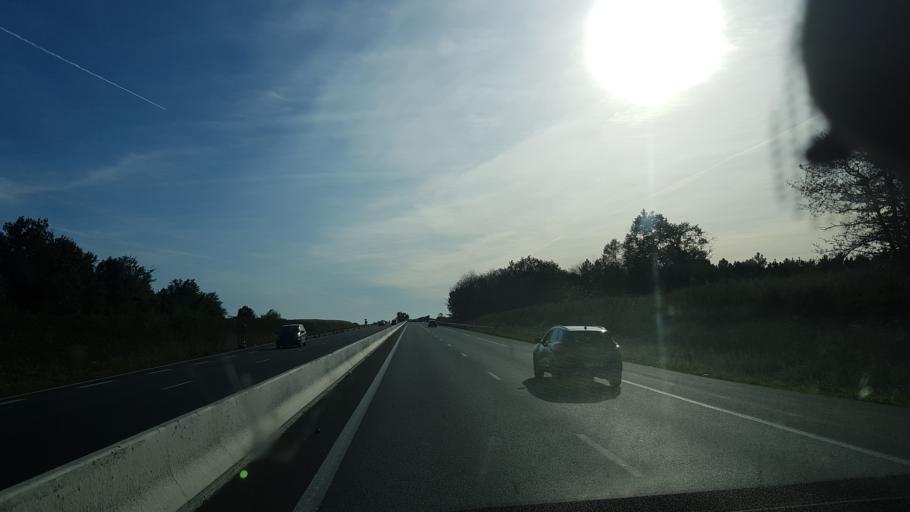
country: FR
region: Poitou-Charentes
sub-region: Departement de la Charente-Maritime
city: Chevanceaux
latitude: 45.3297
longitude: -0.2251
